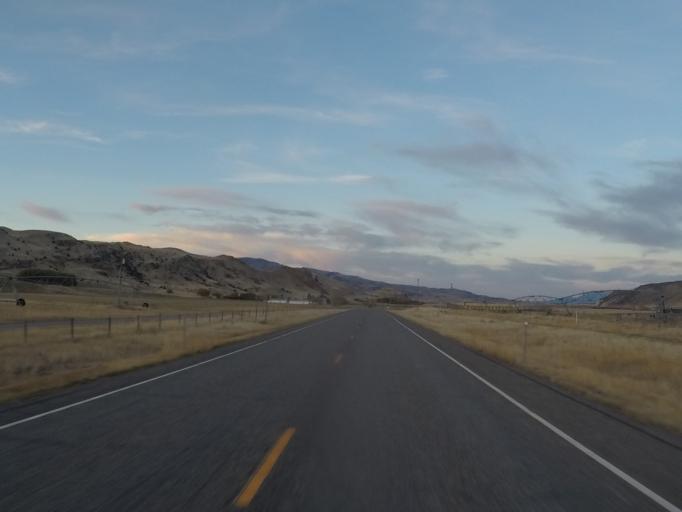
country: US
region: Montana
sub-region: Gallatin County
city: Bozeman
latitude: 45.2705
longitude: -110.8604
